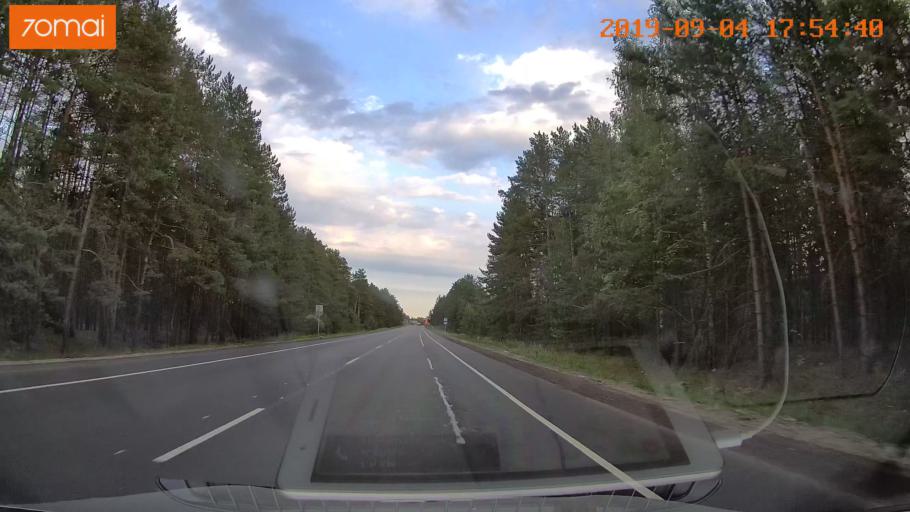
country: RU
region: Moskovskaya
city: Imeni Tsyurupy
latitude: 55.5092
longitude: 38.7509
